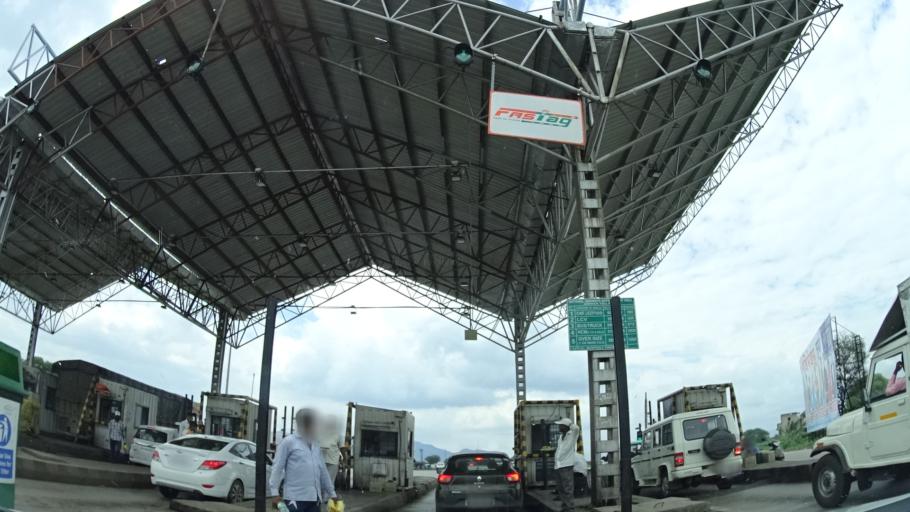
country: IN
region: Maharashtra
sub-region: Satara Division
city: Satara
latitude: 17.8121
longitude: 73.9704
